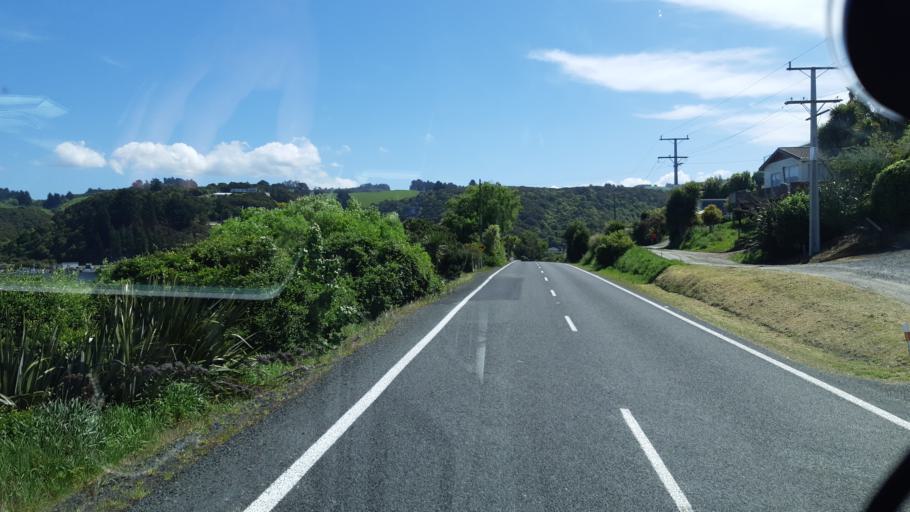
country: NZ
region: Otago
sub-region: Clutha District
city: Milton
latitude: -46.0510
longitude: 170.1975
